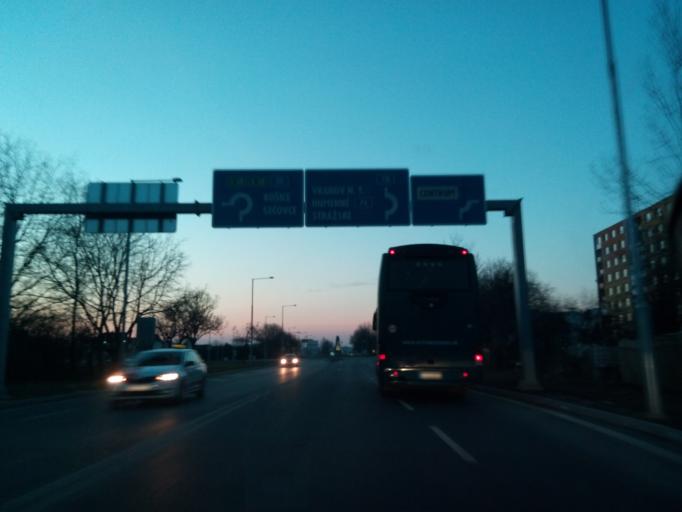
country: SK
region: Kosicky
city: Michalovce
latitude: 48.7482
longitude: 21.9073
